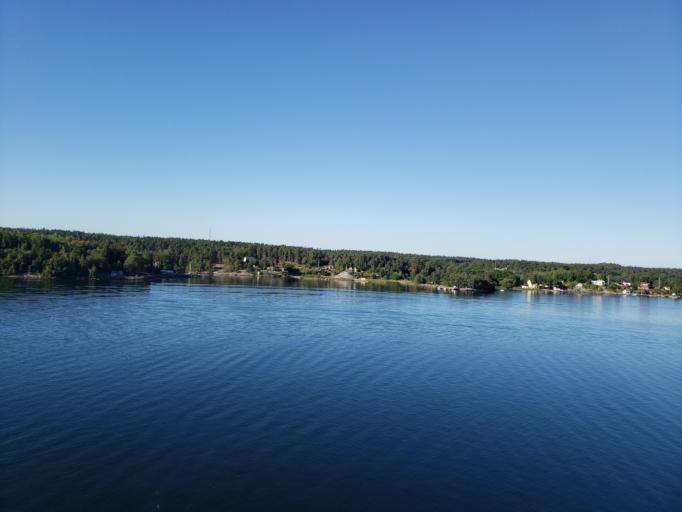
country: SE
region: Stockholm
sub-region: Vaxholms Kommun
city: Vaxholm
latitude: 59.4058
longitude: 18.4274
